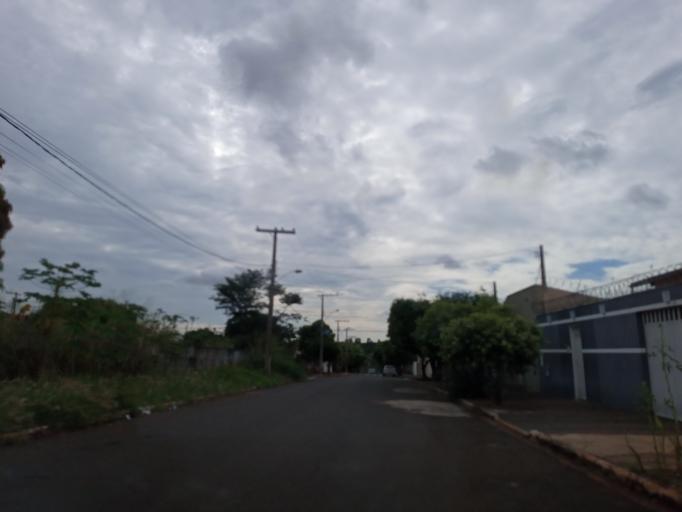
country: BR
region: Minas Gerais
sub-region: Ituiutaba
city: Ituiutaba
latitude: -18.9722
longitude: -49.4740
